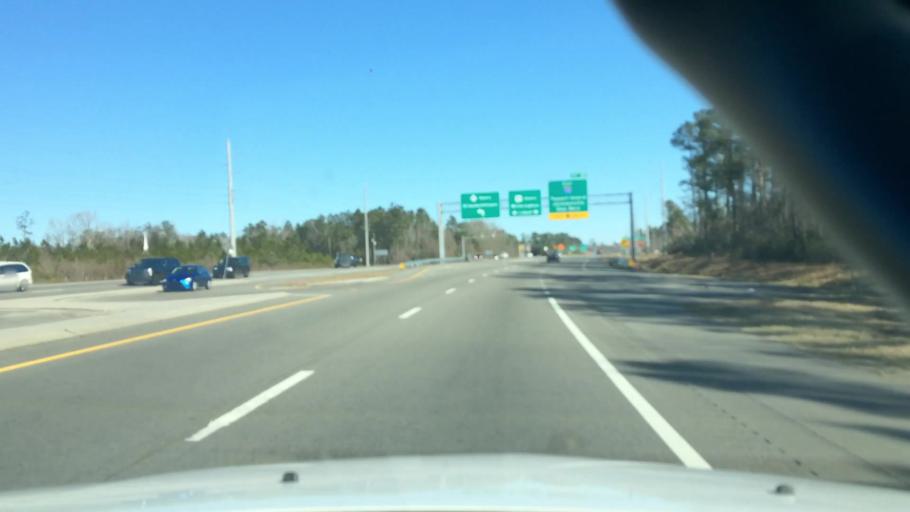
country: US
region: North Carolina
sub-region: Brunswick County
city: Leland
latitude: 34.1771
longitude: -78.0860
